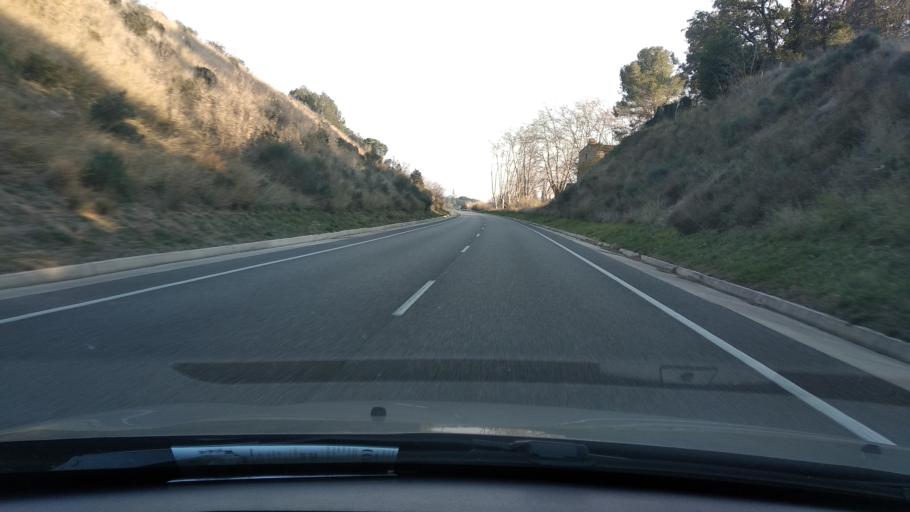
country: ES
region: Catalonia
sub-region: Provincia de Tarragona
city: les Borges del Camp
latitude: 41.1879
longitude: 1.0027
